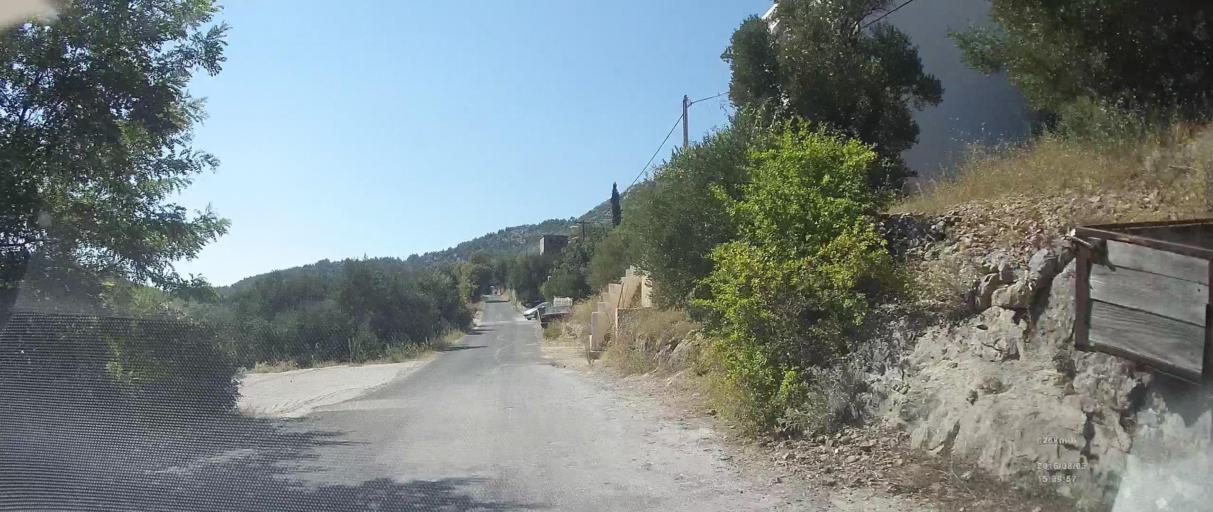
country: HR
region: Dubrovacko-Neretvanska
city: Blato
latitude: 42.7379
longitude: 17.5432
